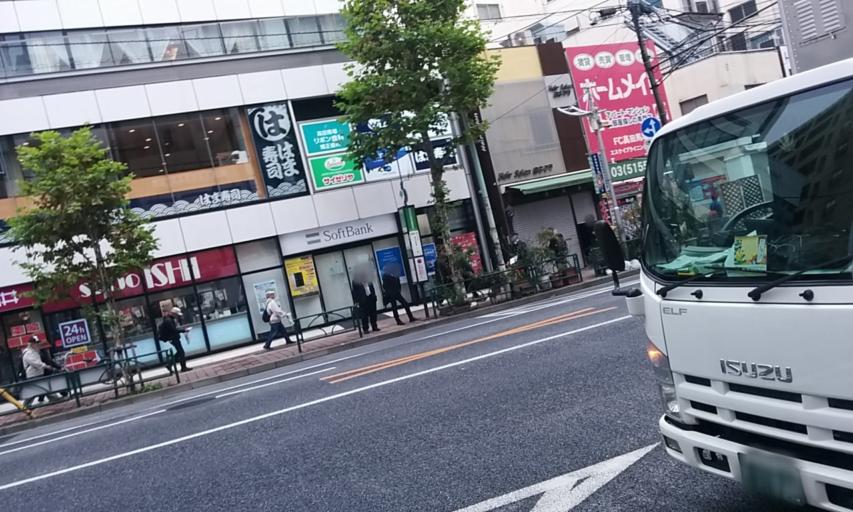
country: JP
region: Tokyo
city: Tokyo
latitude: 35.7121
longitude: 139.7074
